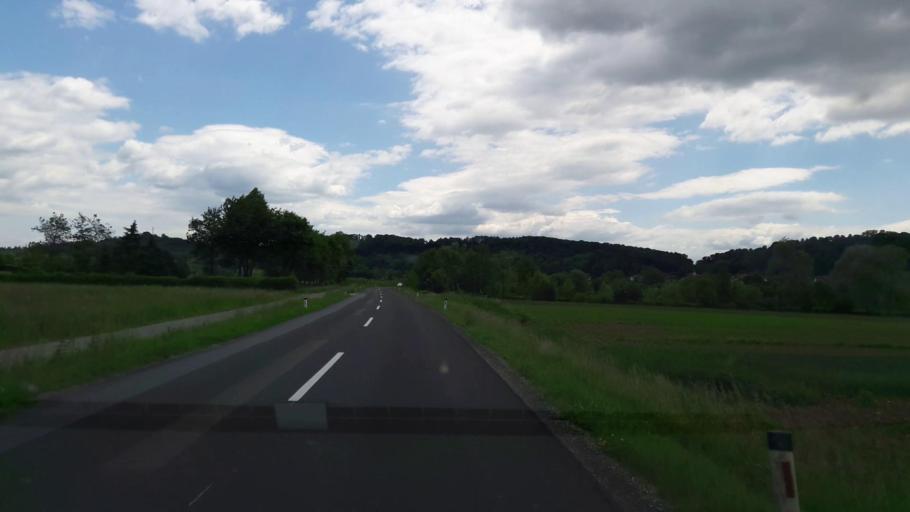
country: AT
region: Styria
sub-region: Politischer Bezirk Hartberg-Fuerstenfeld
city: Soechau
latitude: 47.0699
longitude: 16.0027
